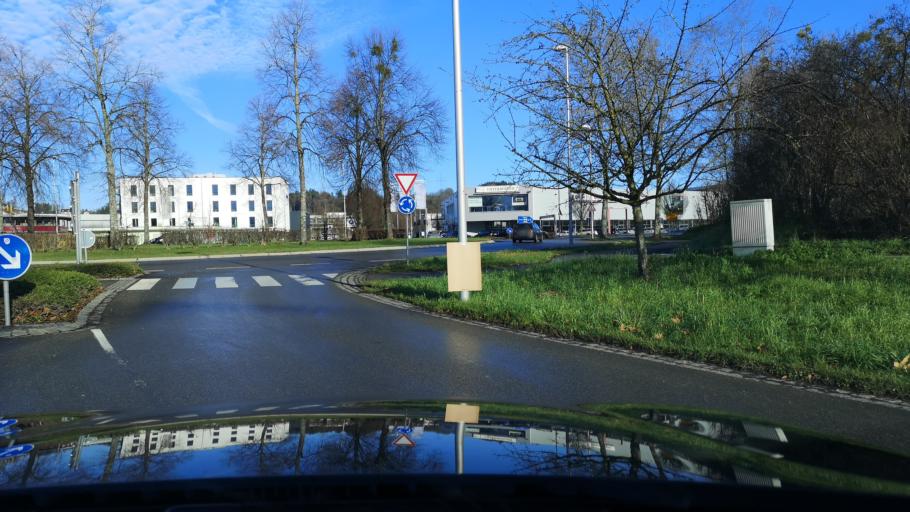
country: AT
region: Vorarlberg
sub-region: Politischer Bezirk Bregenz
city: Horbranz
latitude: 47.5478
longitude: 9.7286
